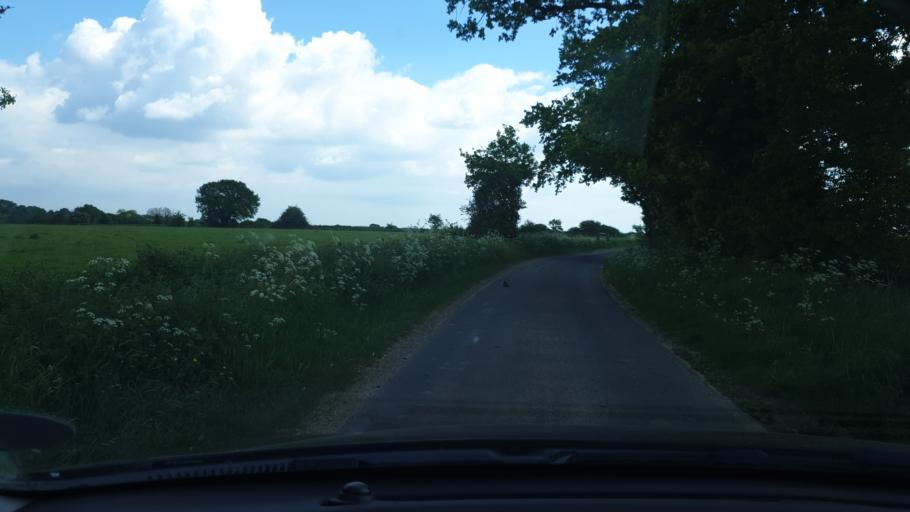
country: GB
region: England
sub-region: Essex
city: Great Bentley
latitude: 51.8497
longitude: 1.0820
